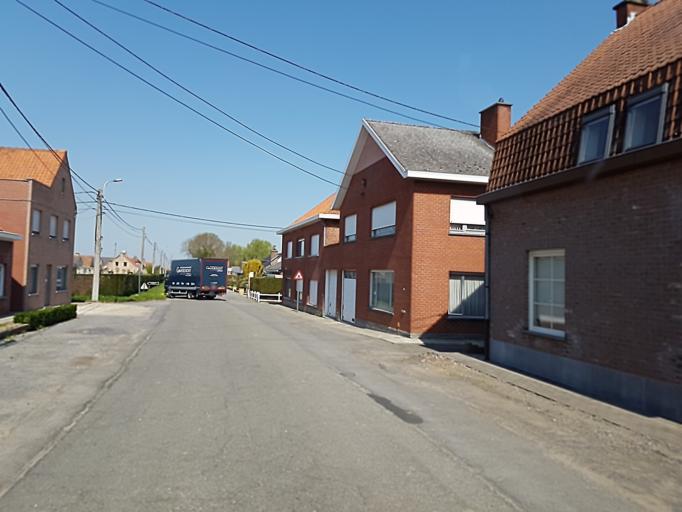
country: BE
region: Flanders
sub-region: Provincie West-Vlaanderen
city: Zonnebeke
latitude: 50.8568
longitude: 2.9599
